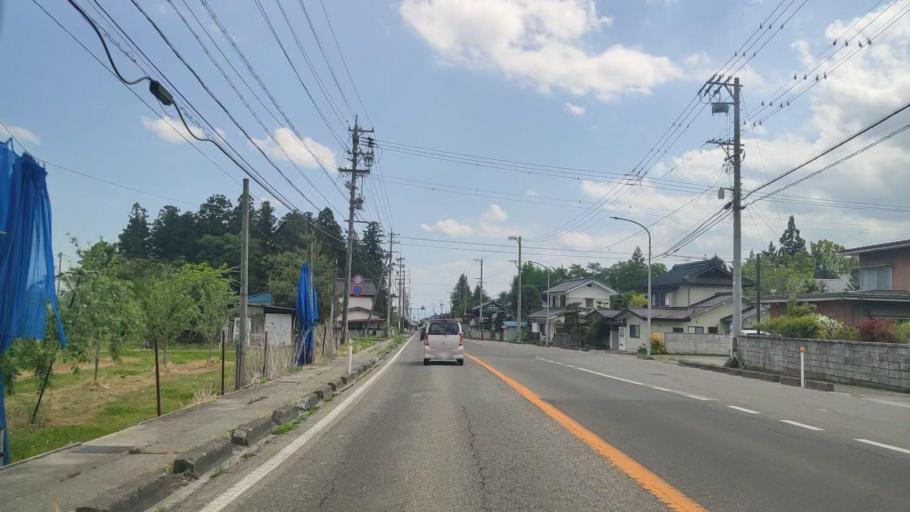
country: JP
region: Nagano
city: Omachi
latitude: 36.4743
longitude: 137.8481
